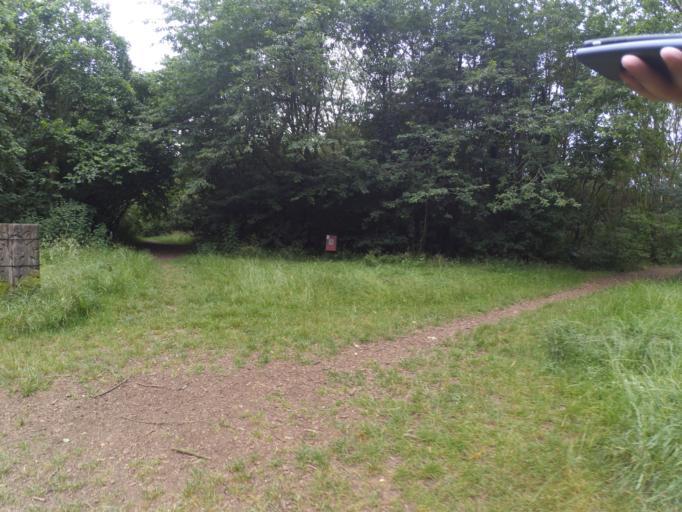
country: GB
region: England
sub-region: Warwickshire
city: Dunchurch
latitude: 52.3486
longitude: -1.2781
